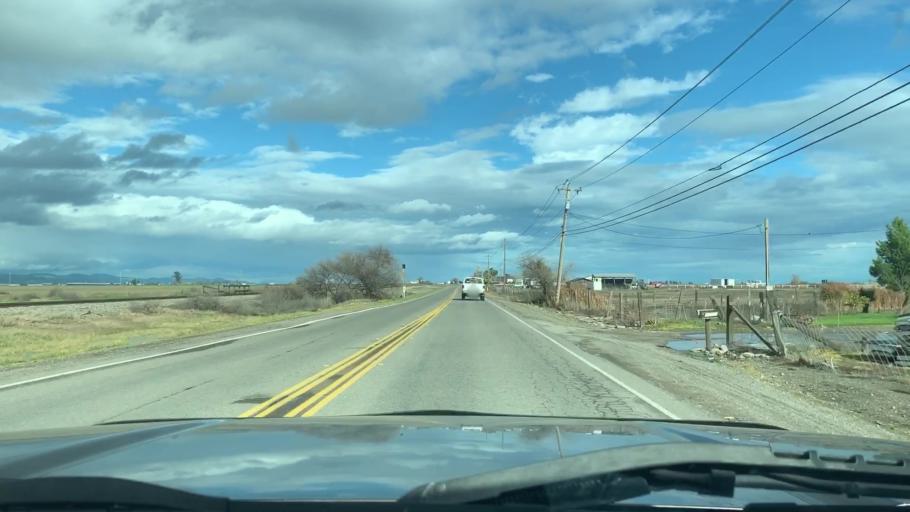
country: US
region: California
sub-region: Merced County
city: Los Banos
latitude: 37.1176
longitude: -120.9442
